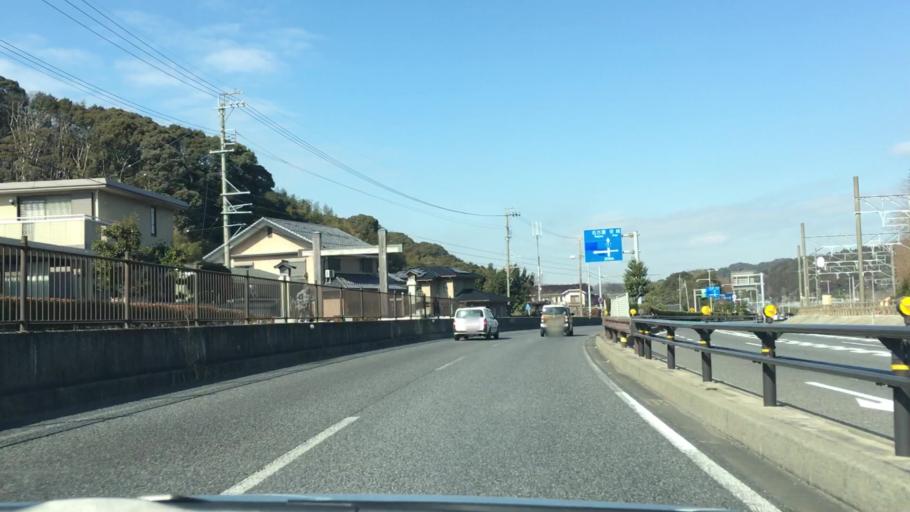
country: JP
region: Aichi
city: Gamagori
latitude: 34.8846
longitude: 137.2654
